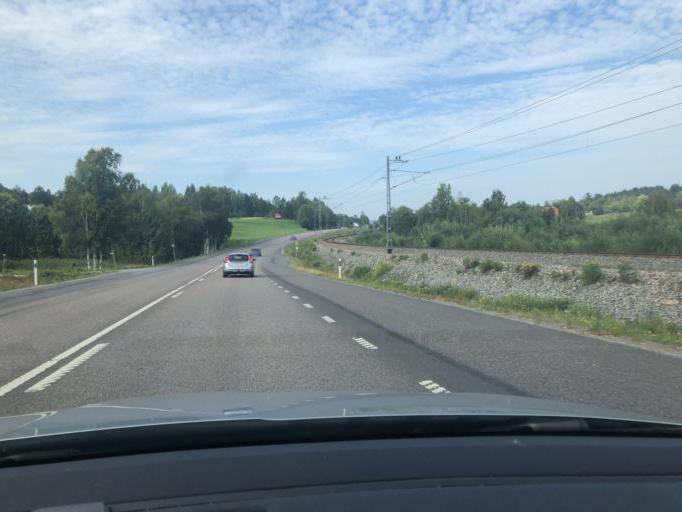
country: SE
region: Vaesternorrland
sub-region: Kramfors Kommun
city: Kramfors
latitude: 62.8999
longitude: 17.8402
